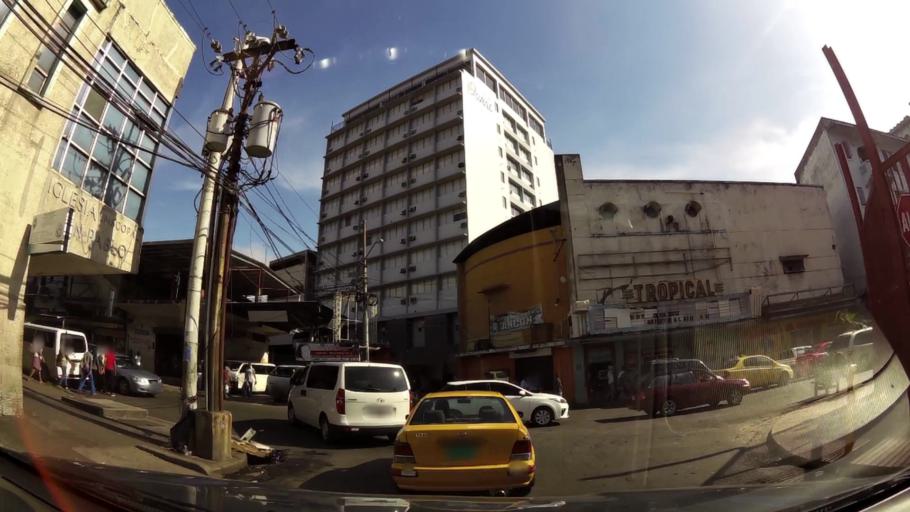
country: PA
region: Panama
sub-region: Distrito de Panama
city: Ancon
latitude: 8.9574
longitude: -79.5419
